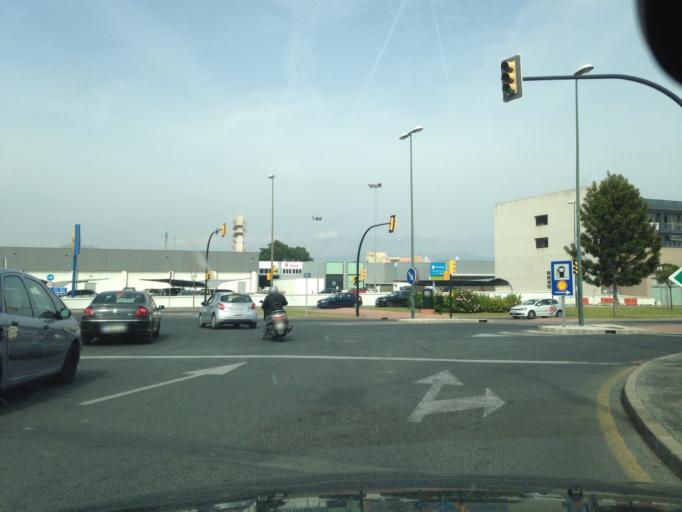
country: ES
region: Andalusia
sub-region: Provincia de Malaga
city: Malaga
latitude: 36.7064
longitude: -4.4714
